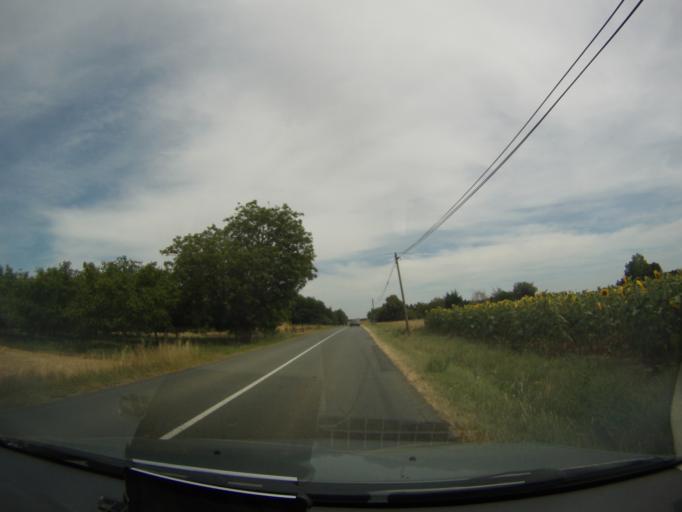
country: FR
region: Poitou-Charentes
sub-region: Departement de la Vienne
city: Mirebeau
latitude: 46.7559
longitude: 0.1641
